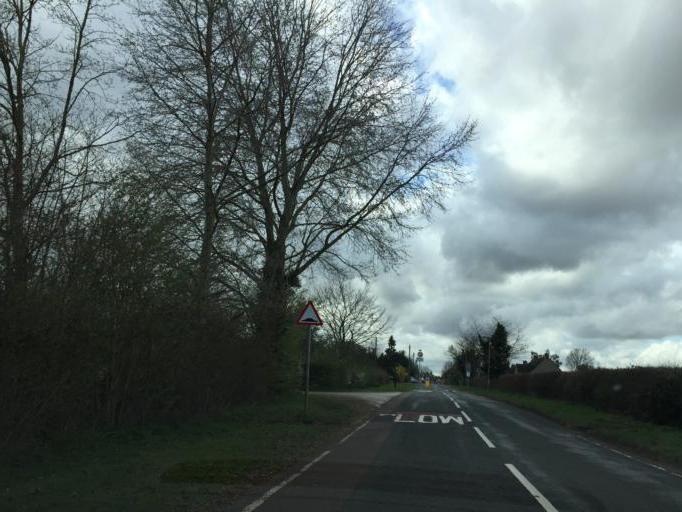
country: GB
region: England
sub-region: Oxfordshire
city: Stonesfield
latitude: 51.8536
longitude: -1.4227
